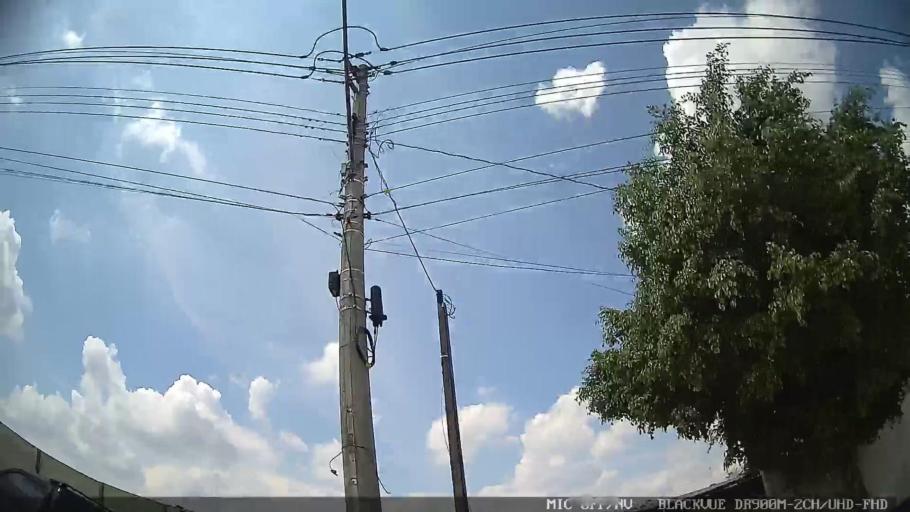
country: BR
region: Sao Paulo
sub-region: Itatiba
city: Itatiba
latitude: -23.0129
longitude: -46.8091
